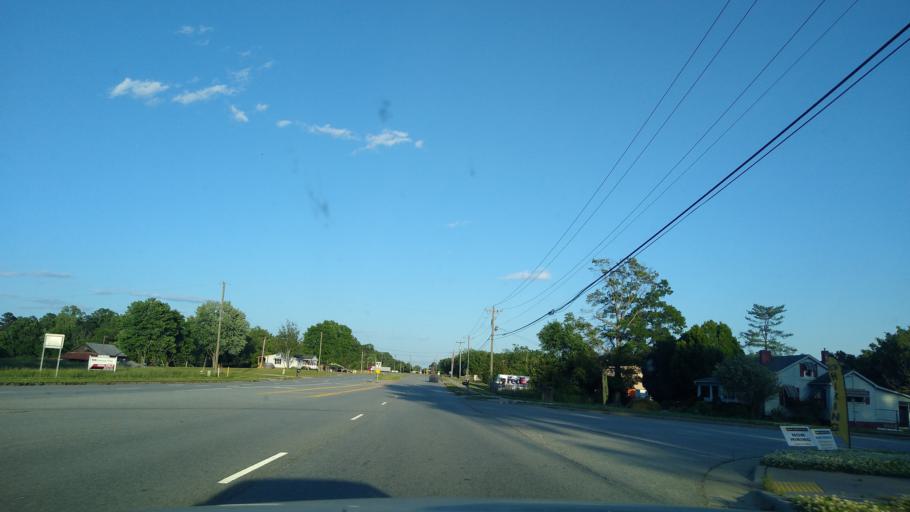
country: US
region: North Carolina
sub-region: Guilford County
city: Oak Ridge
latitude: 36.1037
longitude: -80.0016
